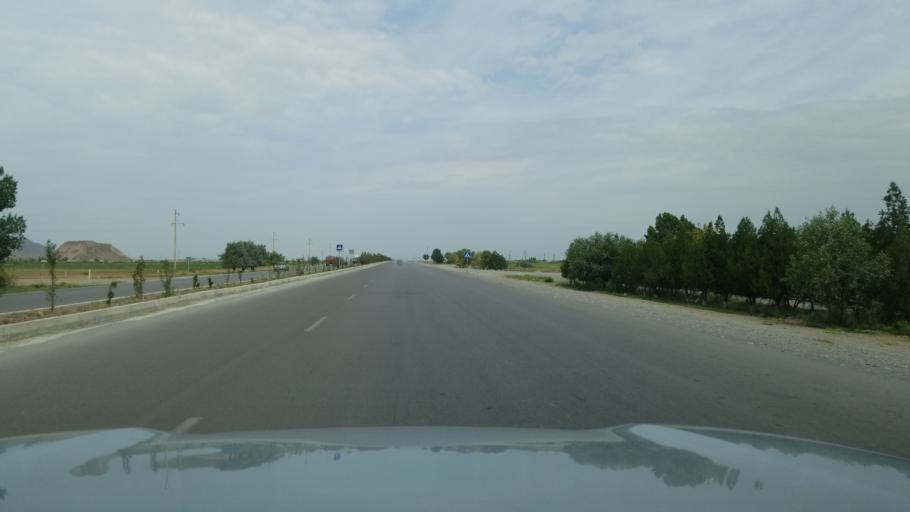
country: TM
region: Ahal
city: Arcabil
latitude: 38.2166
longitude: 57.8061
